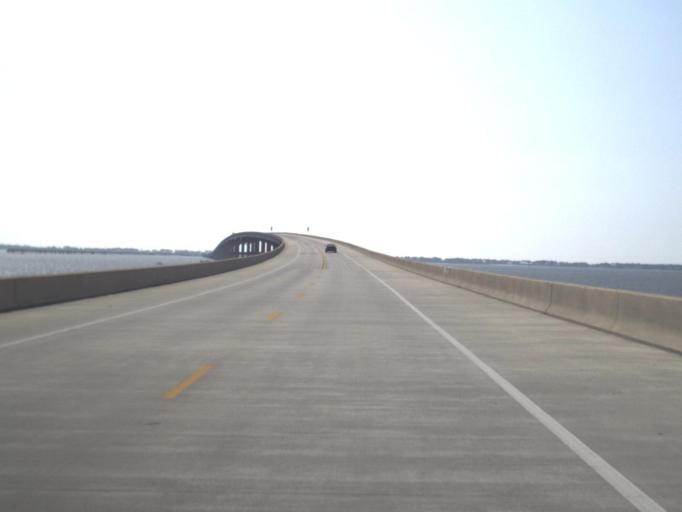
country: US
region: Florida
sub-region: Franklin County
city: Eastpoint
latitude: 29.6894
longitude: -84.8857
